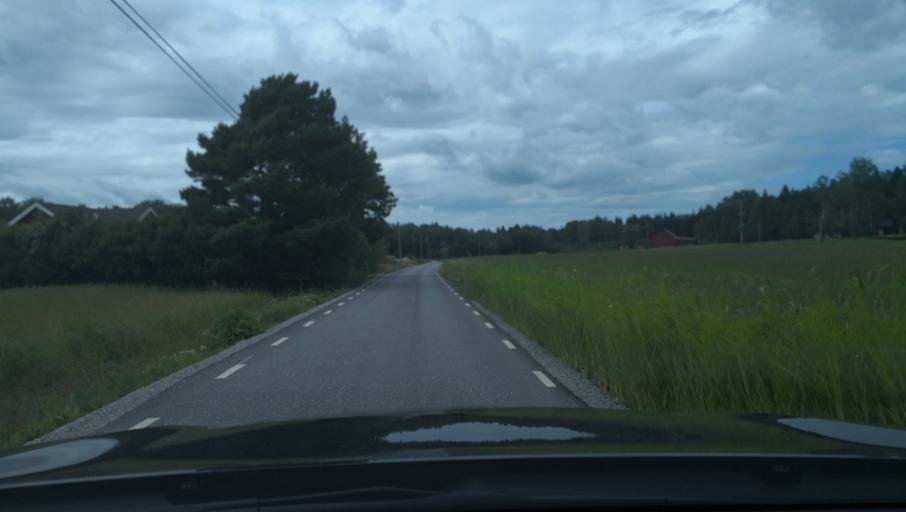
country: SE
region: Vaestmanland
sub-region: Hallstahammars Kommun
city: Hallstahammar
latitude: 59.6160
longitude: 16.1431
